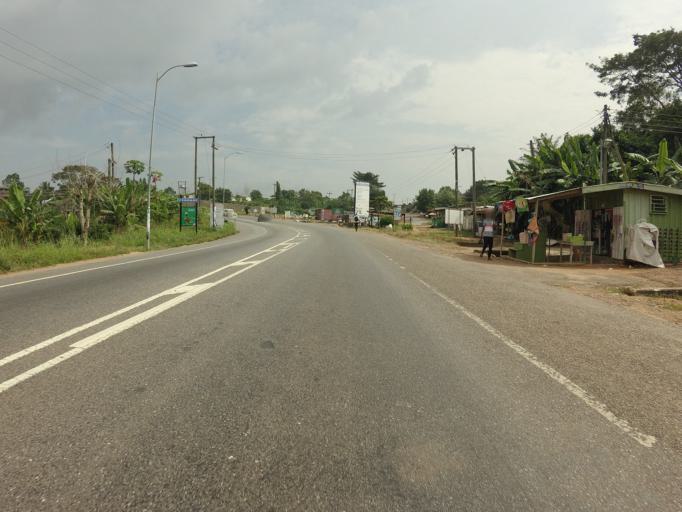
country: GH
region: Eastern
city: Aburi
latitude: 5.8081
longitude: -0.1838
